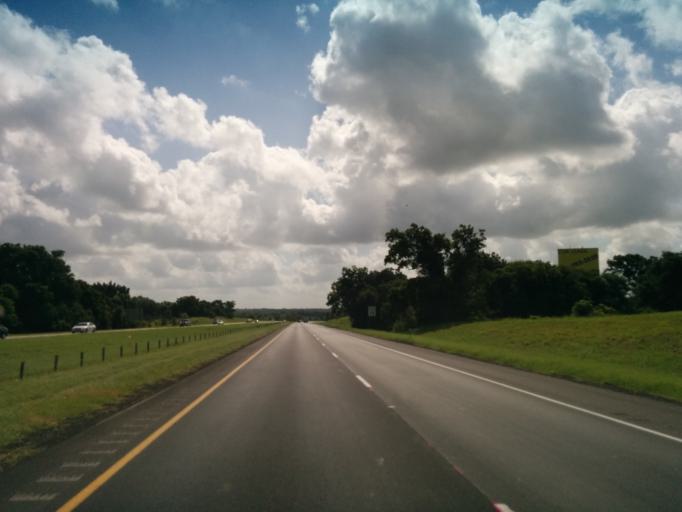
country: US
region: Texas
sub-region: Fayette County
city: Schulenburg
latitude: 29.6951
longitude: -96.8910
